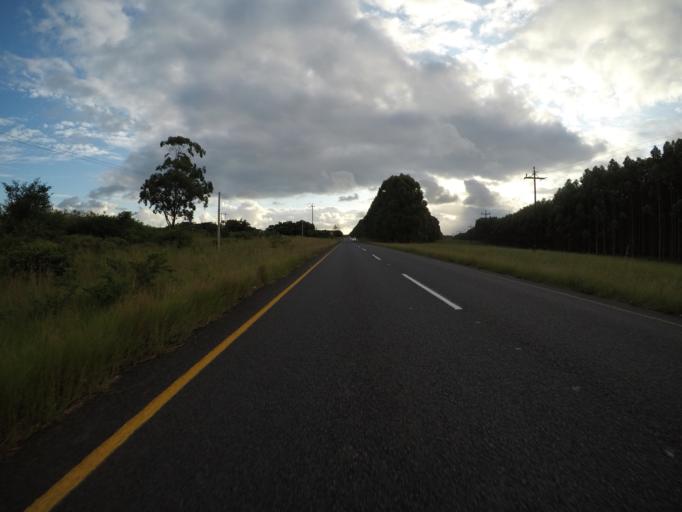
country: ZA
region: KwaZulu-Natal
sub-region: uMkhanyakude District Municipality
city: Mtubatuba
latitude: -28.3958
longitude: 32.2181
